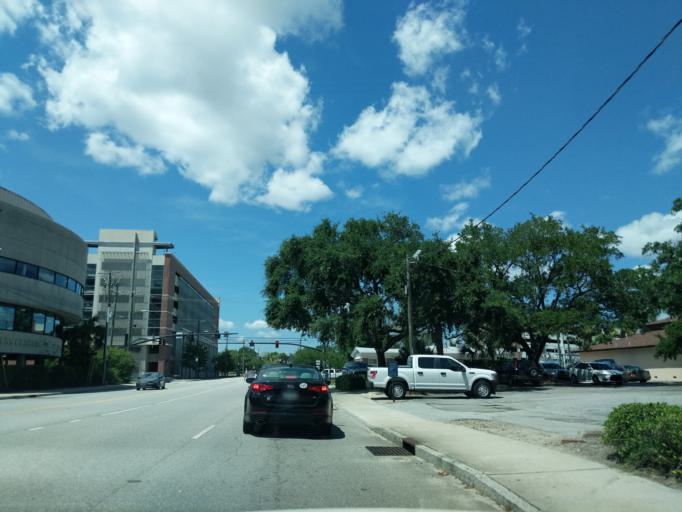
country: US
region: South Carolina
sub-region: Charleston County
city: Charleston
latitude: 32.7850
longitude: -79.9516
